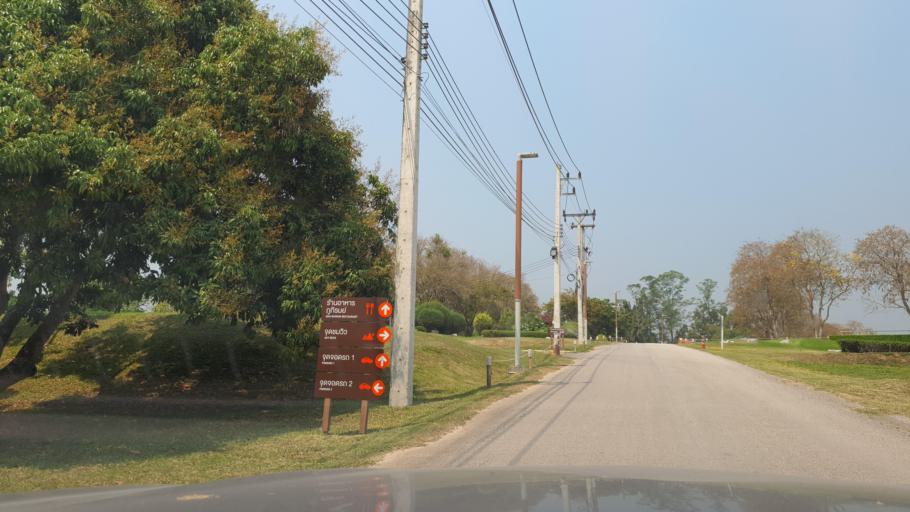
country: TH
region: Chiang Rai
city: Mae Lao
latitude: 19.8614
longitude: 99.7297
